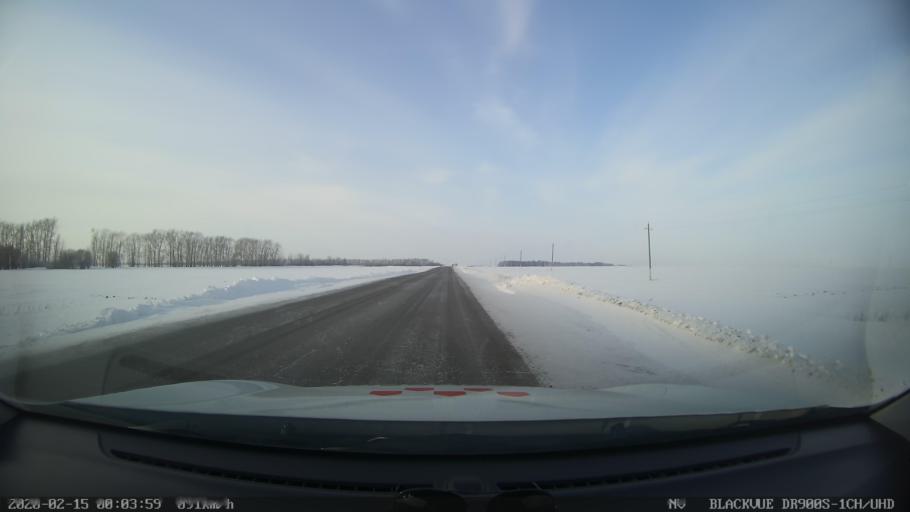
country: RU
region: Tatarstan
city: Kuybyshevskiy Zaton
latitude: 55.3779
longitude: 48.9899
